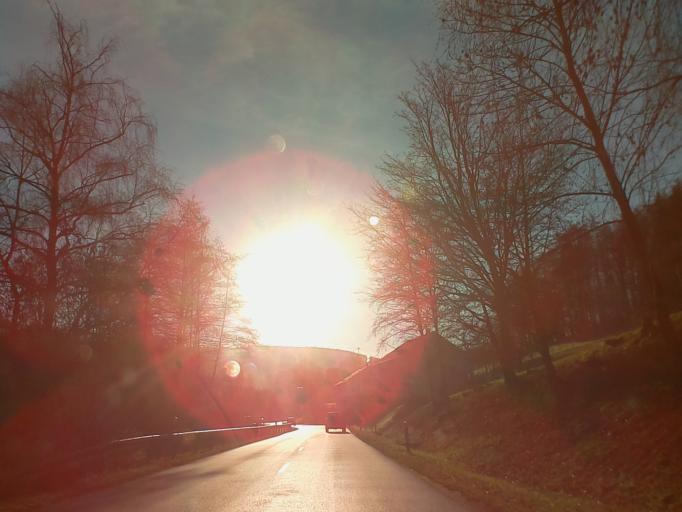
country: DE
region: Hesse
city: Reichelsheim
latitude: 49.6895
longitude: 8.8699
